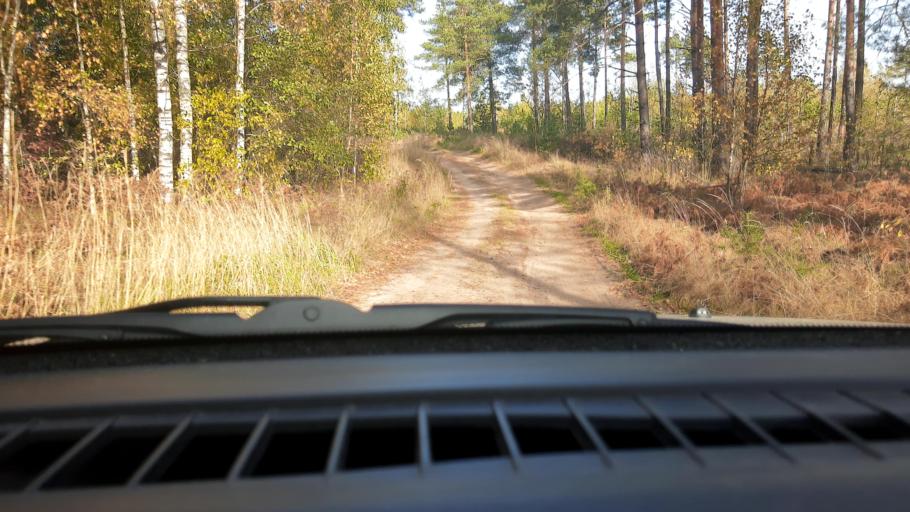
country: RU
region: Nizjnij Novgorod
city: Lukino
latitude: 56.3883
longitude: 43.6284
